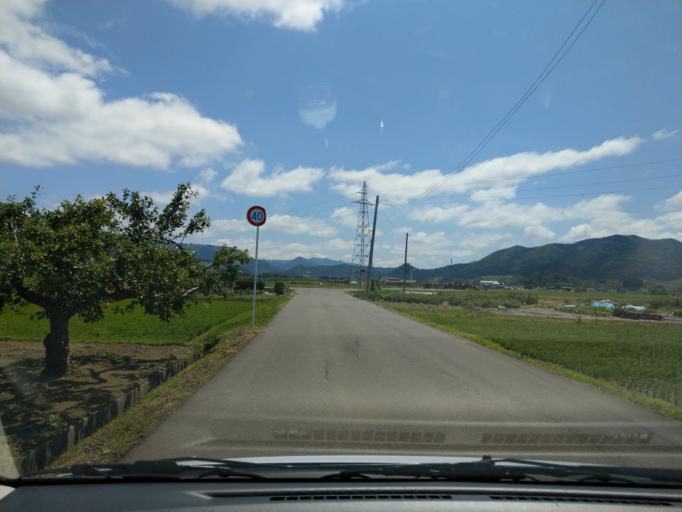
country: JP
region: Aomori
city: Hirosaki
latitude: 40.5621
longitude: 140.5516
